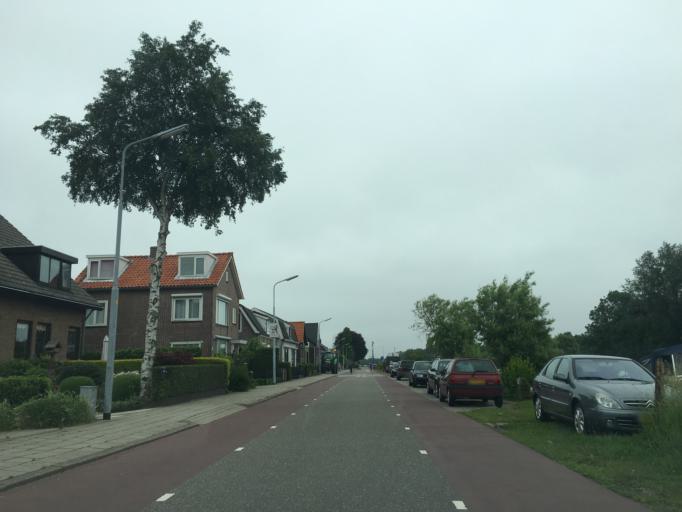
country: NL
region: North Holland
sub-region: Gemeente Aalsmeer
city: Aalsmeer
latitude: 52.2746
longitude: 4.7563
